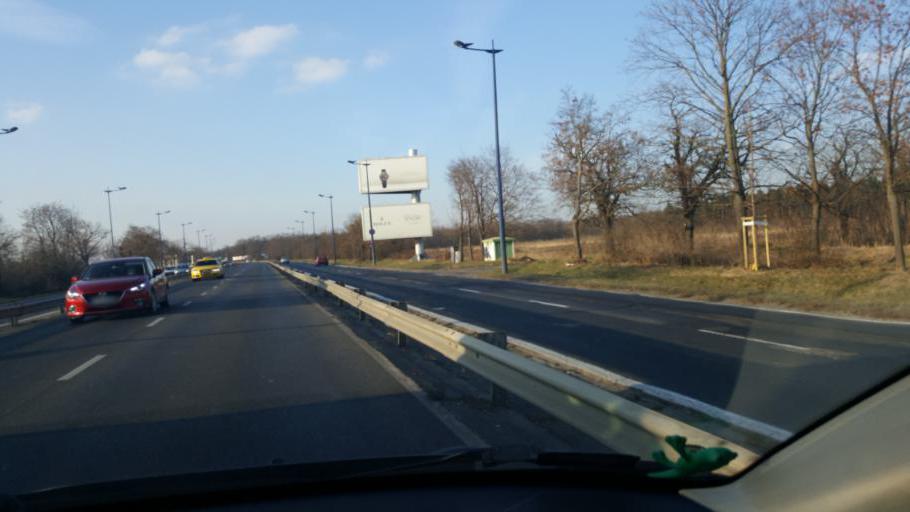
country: HU
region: Budapest
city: Budapest XVIII. keruelet
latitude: 47.4489
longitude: 19.2052
